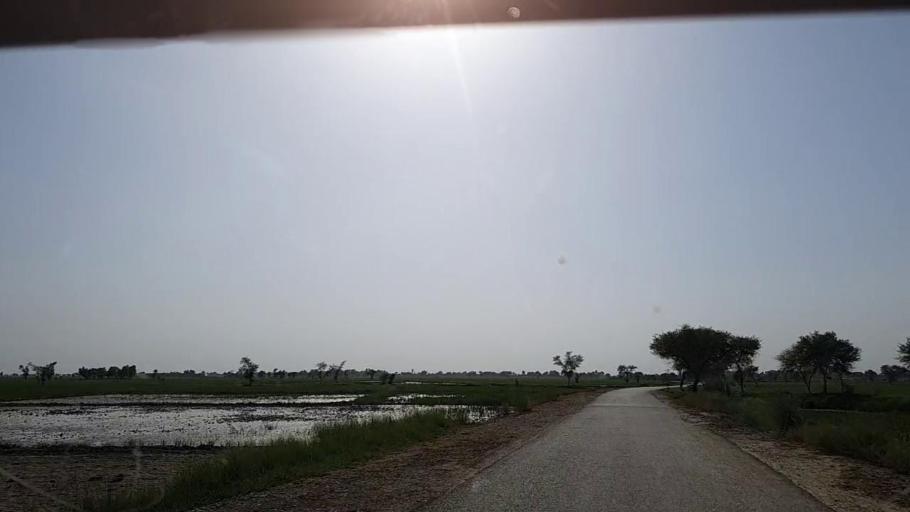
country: PK
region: Sindh
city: Phulji
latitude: 26.9878
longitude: 67.6580
